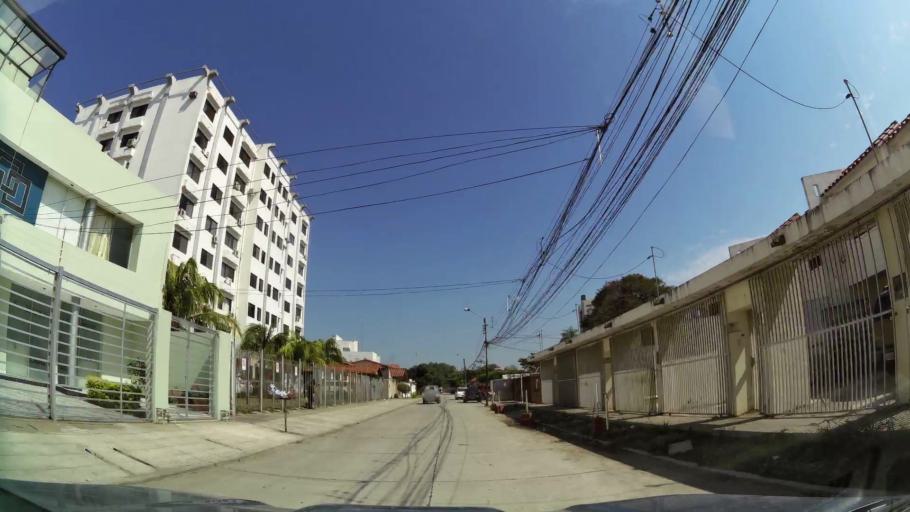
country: BO
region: Santa Cruz
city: Santa Cruz de la Sierra
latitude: -17.7504
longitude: -63.1657
